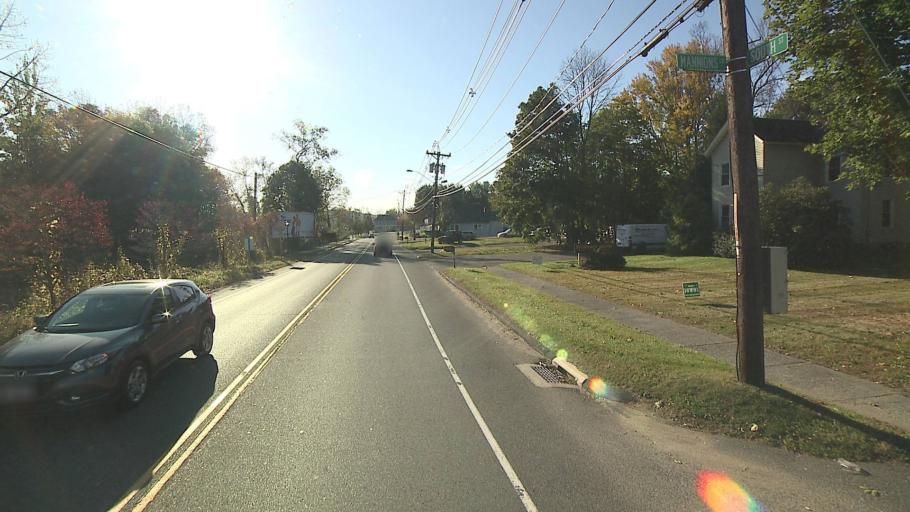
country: US
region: Connecticut
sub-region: Fairfield County
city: Bethel
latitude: 41.3844
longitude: -73.4262
